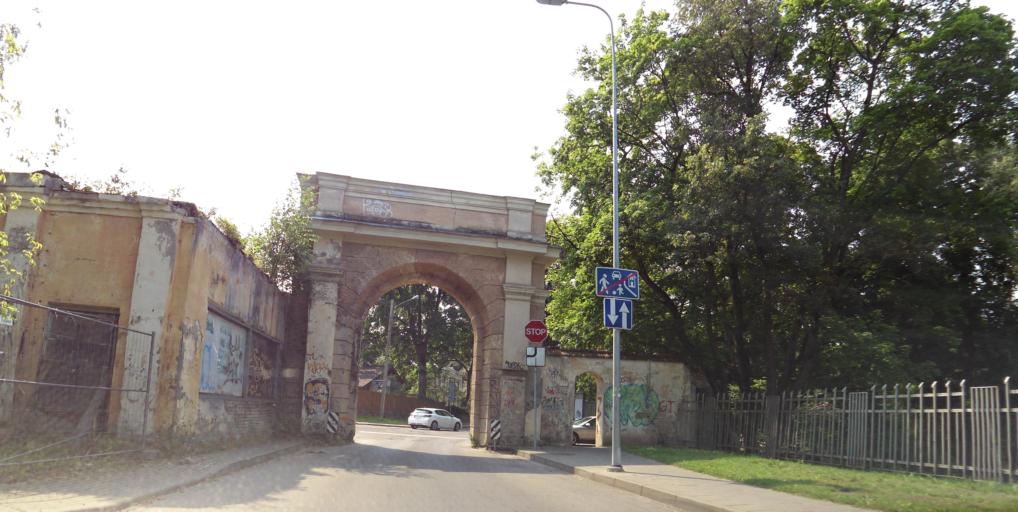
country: LT
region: Vilnius County
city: Rasos
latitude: 54.6984
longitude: 25.3132
